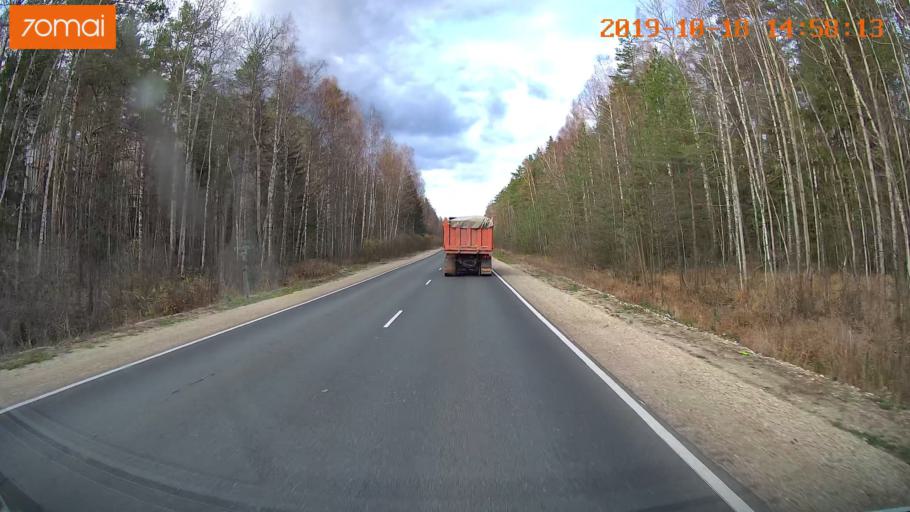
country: RU
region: Vladimir
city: Kurlovo
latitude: 55.4881
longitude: 40.5780
